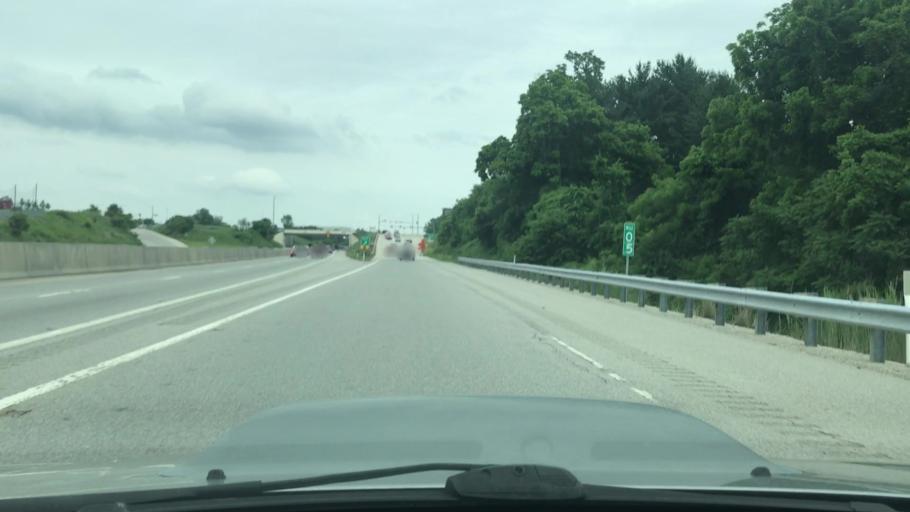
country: US
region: Pennsylvania
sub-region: Montgomery County
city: Wyncote
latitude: 40.0898
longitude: -75.1675
